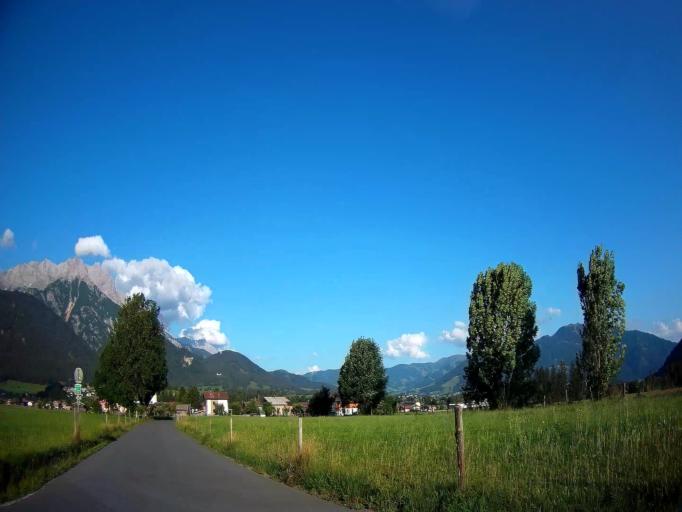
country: AT
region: Salzburg
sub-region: Politischer Bezirk Zell am See
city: Saalfelden am Steinernen Meer
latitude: 47.4489
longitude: 12.8111
